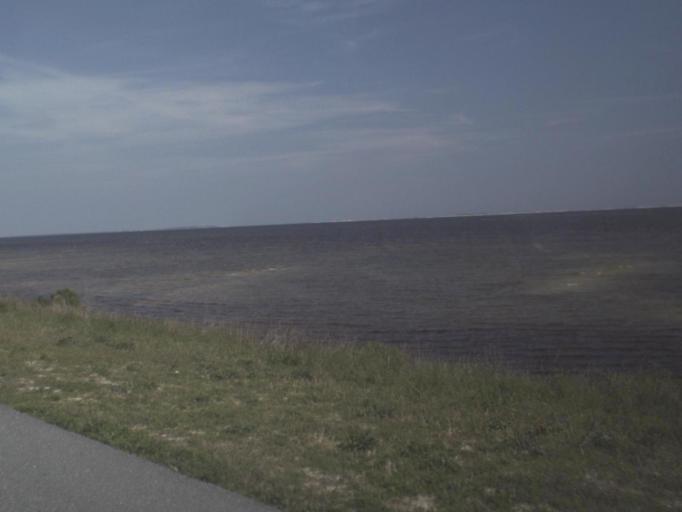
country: US
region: Florida
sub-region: Franklin County
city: Eastpoint
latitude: 29.7793
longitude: -84.7817
